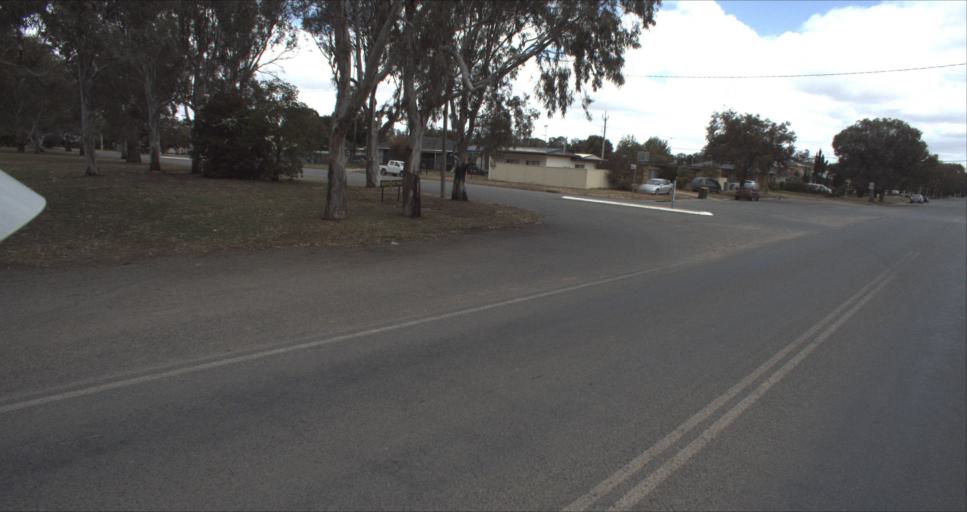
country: AU
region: New South Wales
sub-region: Leeton
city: Leeton
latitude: -34.5536
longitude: 146.3917
